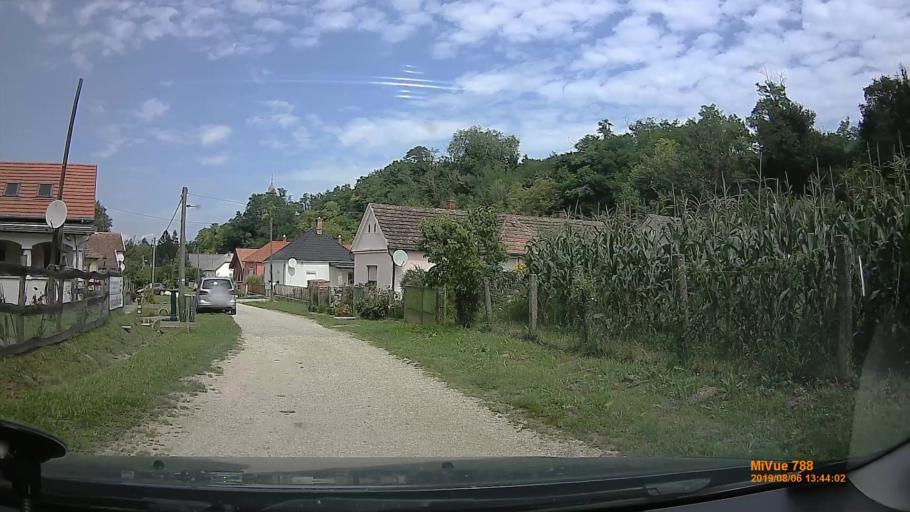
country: HU
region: Zala
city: Zalakomar
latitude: 46.5698
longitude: 17.0935
